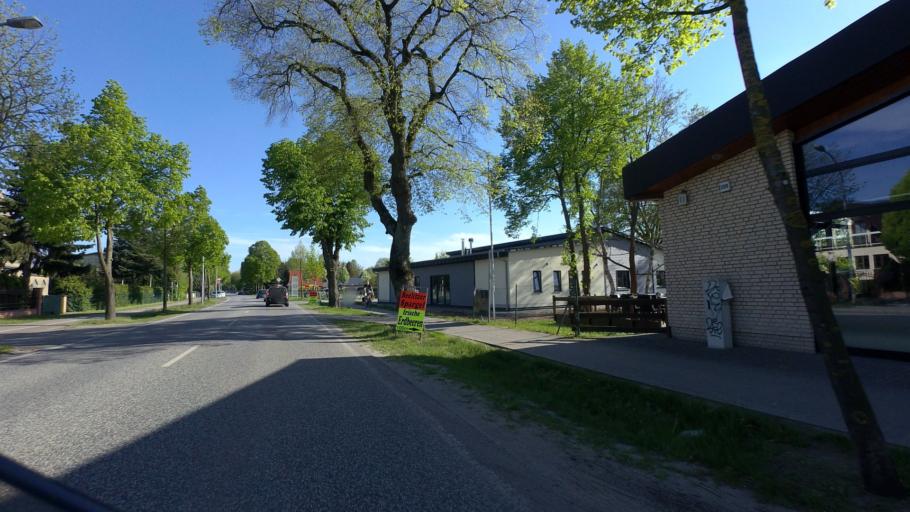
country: DE
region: Brandenburg
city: Oranienburg
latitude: 52.7263
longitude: 13.2478
